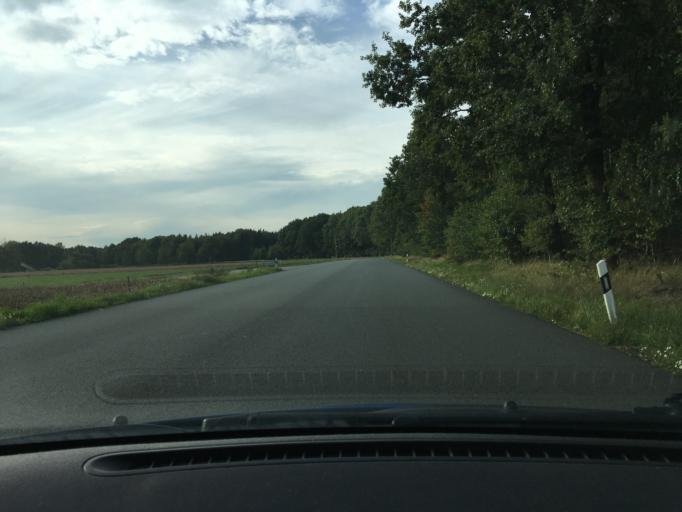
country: DE
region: Lower Saxony
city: Munster
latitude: 52.9167
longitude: 10.0772
